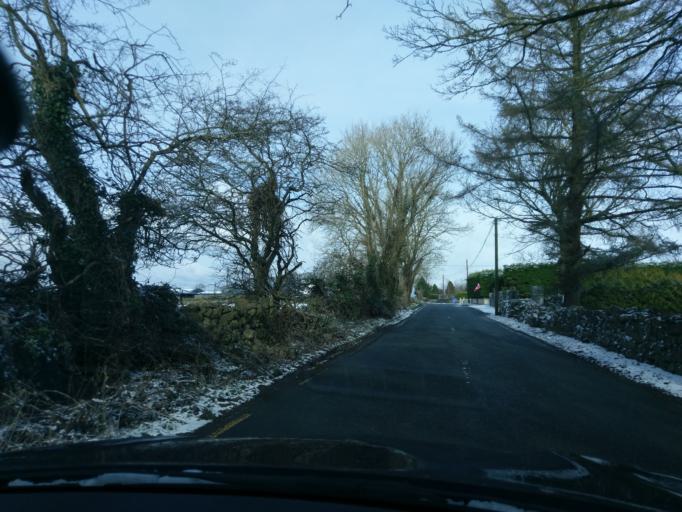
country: IE
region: Connaught
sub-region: County Galway
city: Athenry
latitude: 53.1854
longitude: -8.7708
